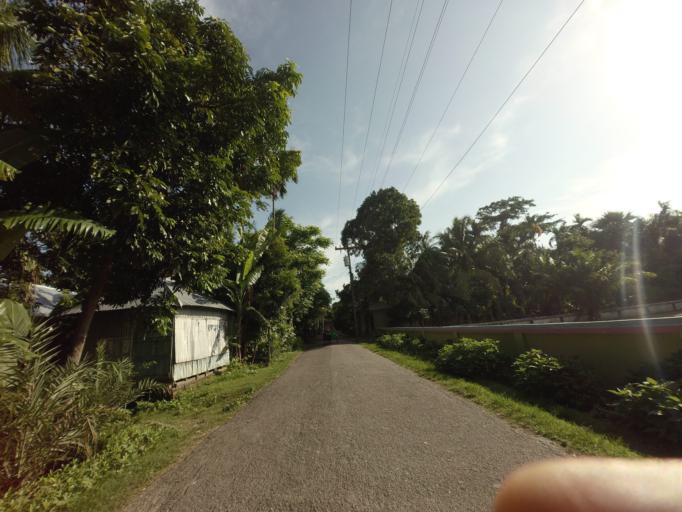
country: BD
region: Khulna
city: Kalia
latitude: 23.0093
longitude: 89.5848
